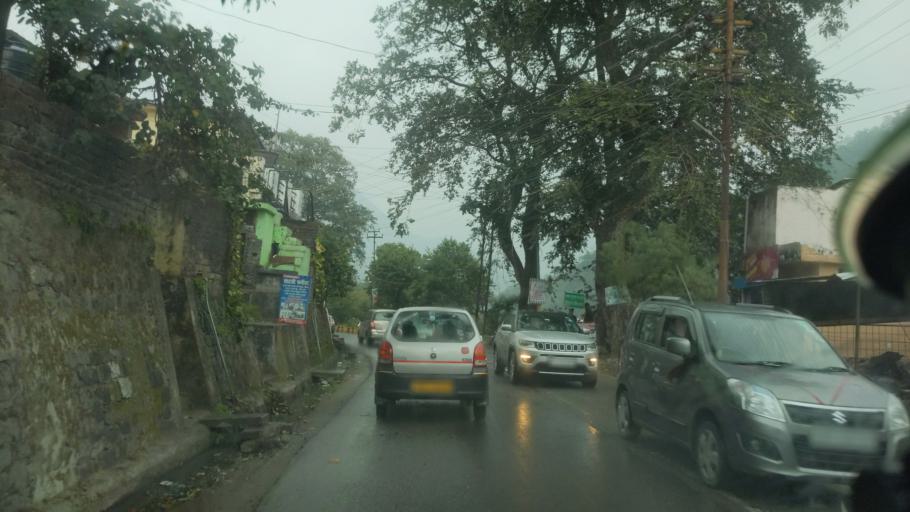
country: IN
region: Uttarakhand
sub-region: Naini Tal
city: Haldwani
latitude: 29.2750
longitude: 79.5454
